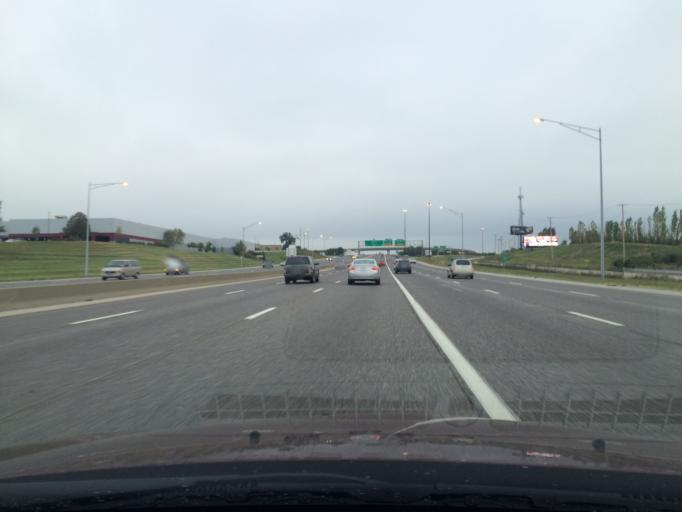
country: US
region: Missouri
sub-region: Saint Louis County
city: Bridgeton
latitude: 38.7522
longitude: -90.4498
